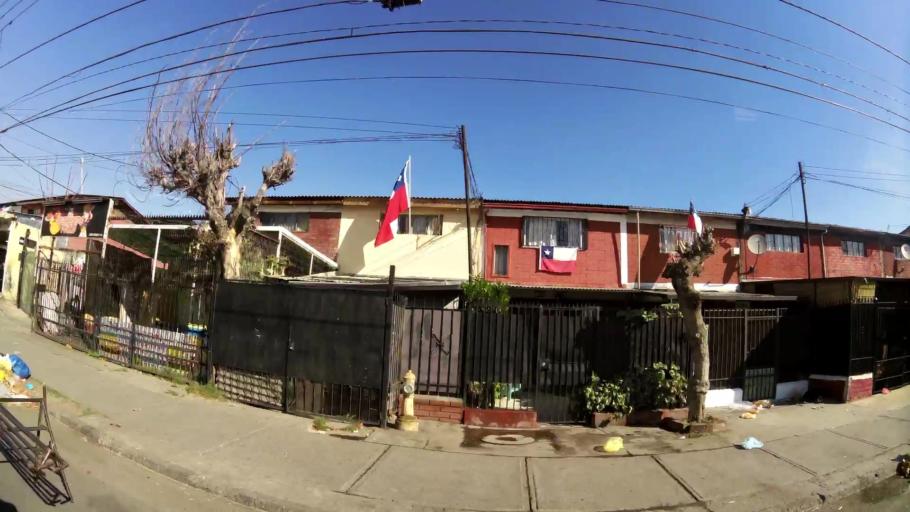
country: CL
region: Santiago Metropolitan
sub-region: Provincia de Santiago
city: La Pintana
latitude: -33.5594
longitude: -70.6067
